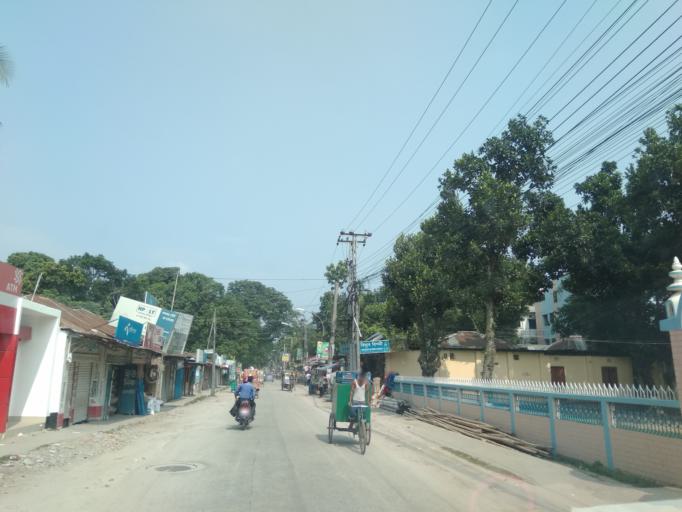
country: BD
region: Rangpur Division
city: Rangpur
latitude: 25.7586
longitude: 89.2344
